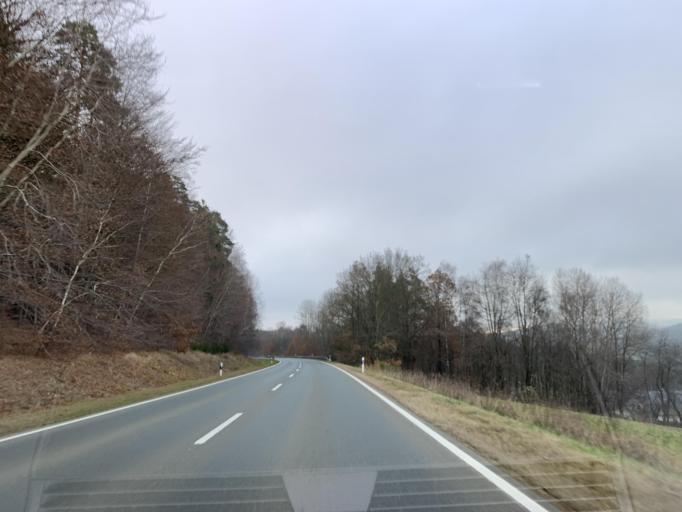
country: DE
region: Bavaria
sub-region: Upper Palatinate
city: Thanstein
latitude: 49.3471
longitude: 12.4666
